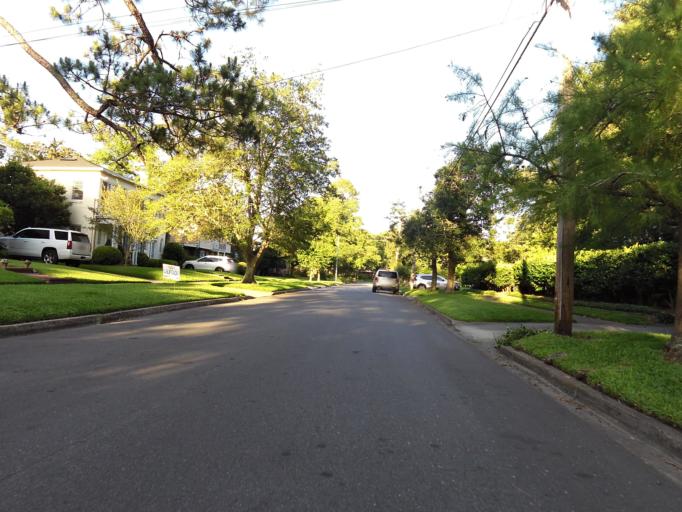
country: US
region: Florida
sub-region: Clay County
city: Orange Park
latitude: 30.2500
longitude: -81.6939
